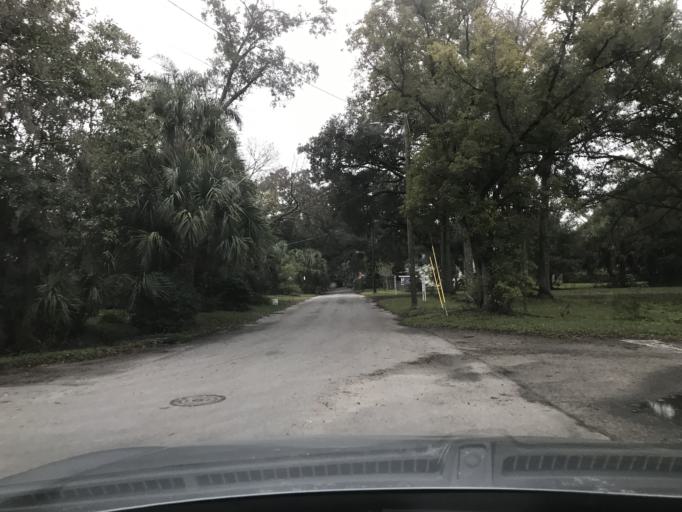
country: US
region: Florida
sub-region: Hillsborough County
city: Tampa
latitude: 27.9841
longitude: -82.4665
